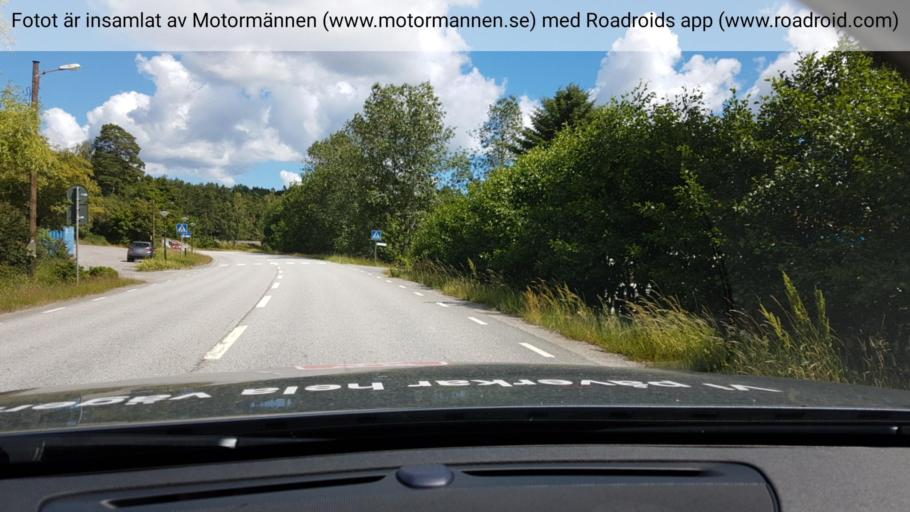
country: SE
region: Stockholm
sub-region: Varmdo Kommun
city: Hemmesta
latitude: 59.3607
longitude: 18.5149
